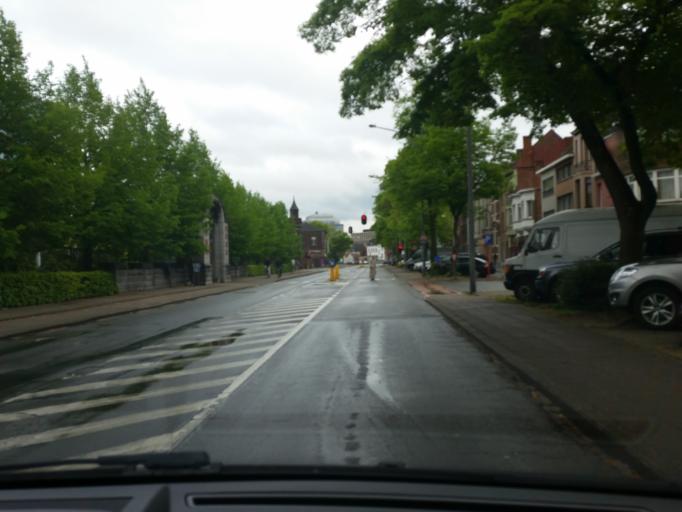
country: BE
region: Flanders
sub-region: Provincie Antwerpen
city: Mechelen
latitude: 51.0355
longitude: 4.4824
